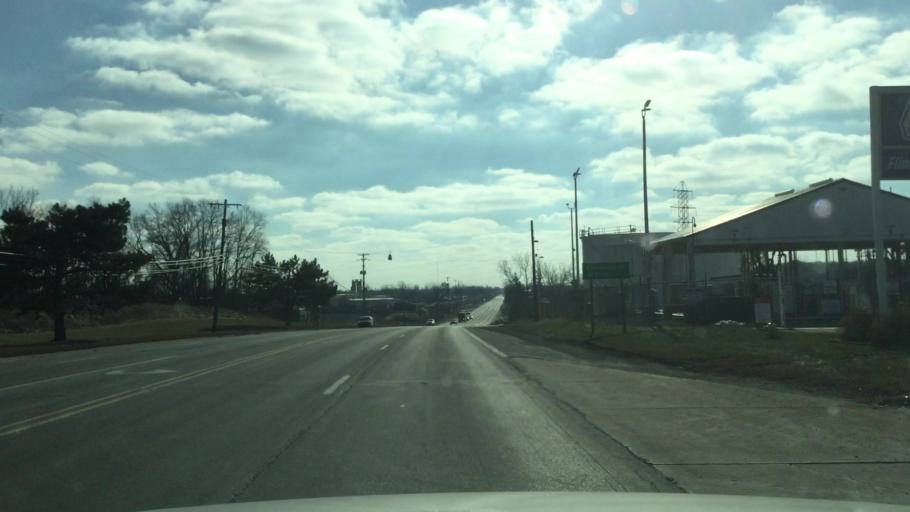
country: US
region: Michigan
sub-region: Genesee County
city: Beecher
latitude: 43.0920
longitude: -83.6747
